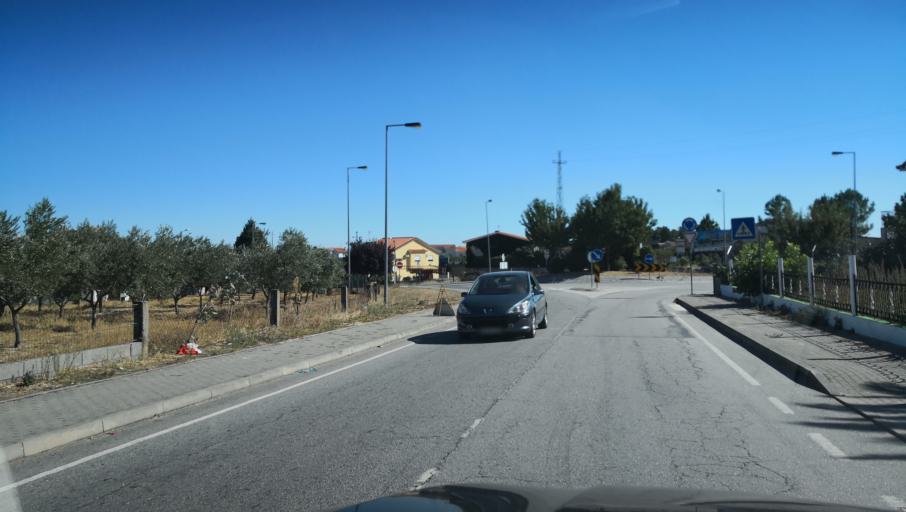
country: PT
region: Vila Real
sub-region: Valpacos
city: Valpacos
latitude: 41.6648
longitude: -7.3335
